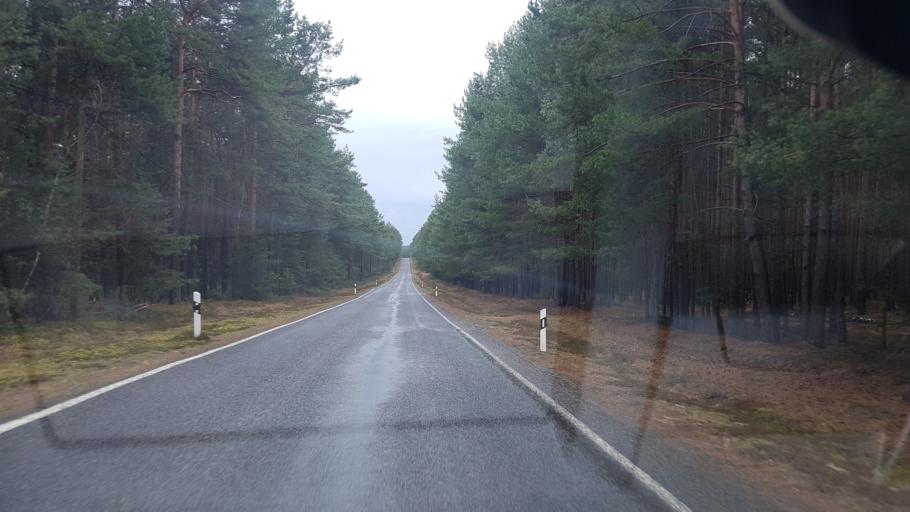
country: DE
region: Brandenburg
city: Neupetershain
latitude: 51.6155
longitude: 14.1086
